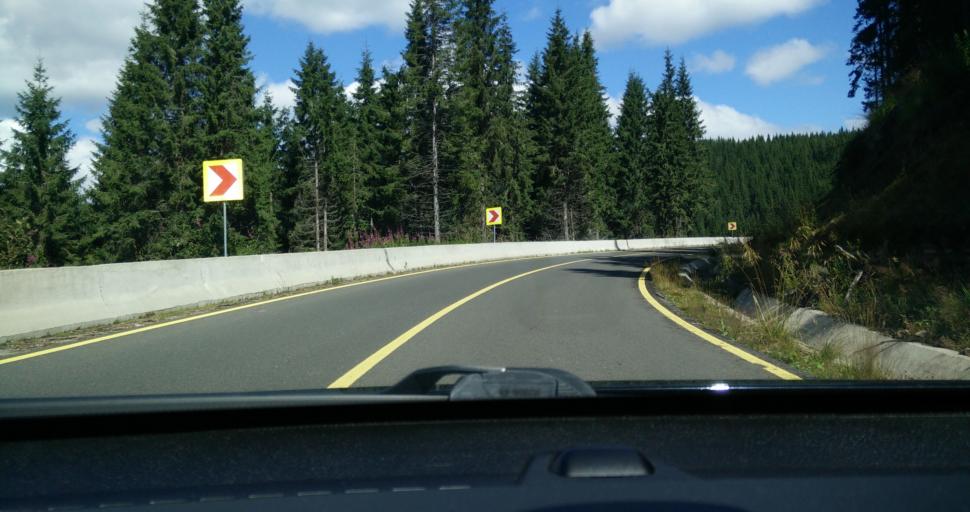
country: RO
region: Hunedoara
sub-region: Oras Petrila
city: Petrila
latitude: 45.4557
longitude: 23.6132
